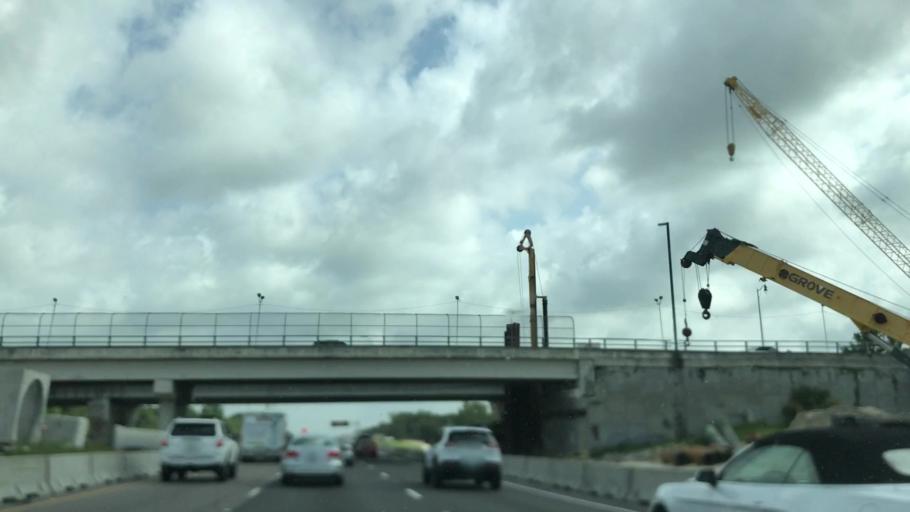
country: US
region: Florida
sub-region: Seminole County
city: Altamonte Springs
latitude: 28.6722
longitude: -81.3884
